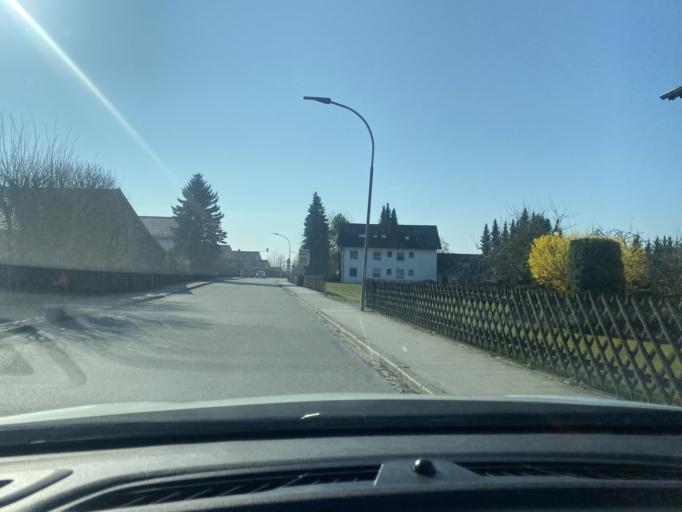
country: DE
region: Bavaria
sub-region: Upper Bavaria
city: Oberding
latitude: 48.3191
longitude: 11.8471
